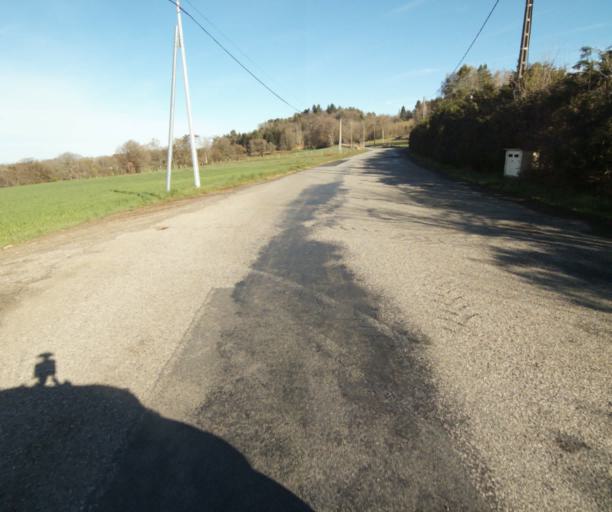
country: FR
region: Limousin
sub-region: Departement de la Correze
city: Laguenne
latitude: 45.2716
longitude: 1.8654
